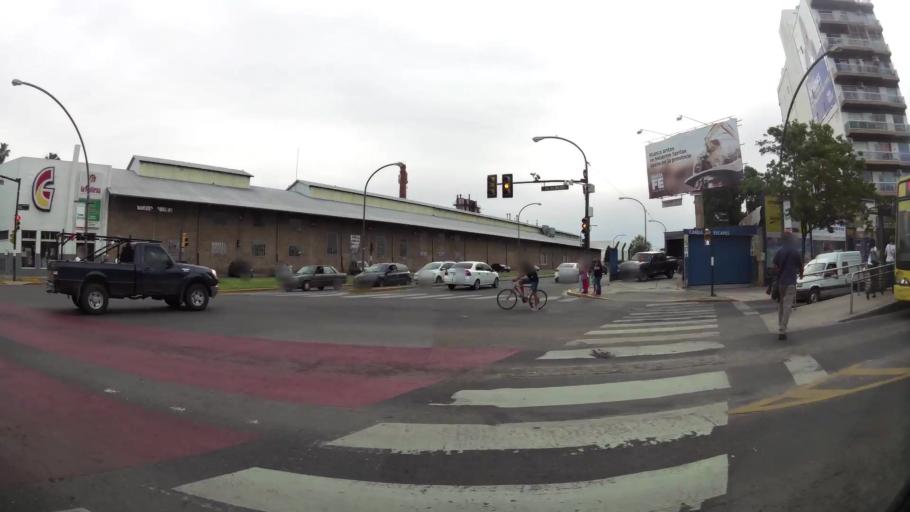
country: AR
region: Santa Fe
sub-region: Departamento de Rosario
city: Rosario
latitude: -32.9219
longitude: -60.6802
